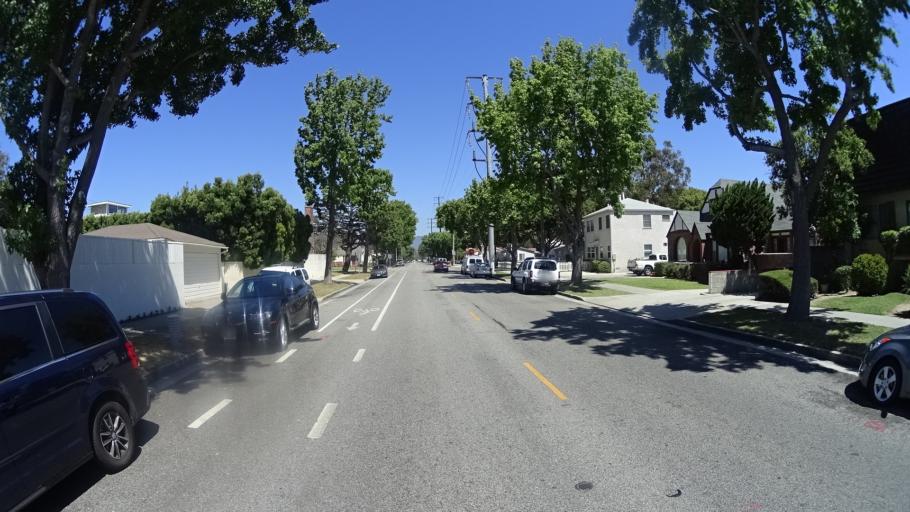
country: US
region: California
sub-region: Los Angeles County
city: Santa Monica
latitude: 34.0128
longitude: -118.4726
